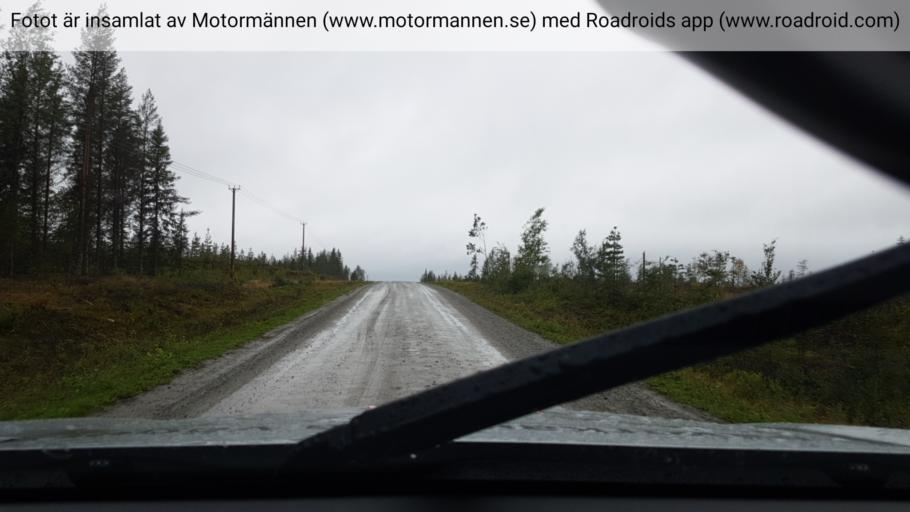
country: SE
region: Vaesterbotten
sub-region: Asele Kommun
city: Insjon
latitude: 64.0865
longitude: 17.7238
